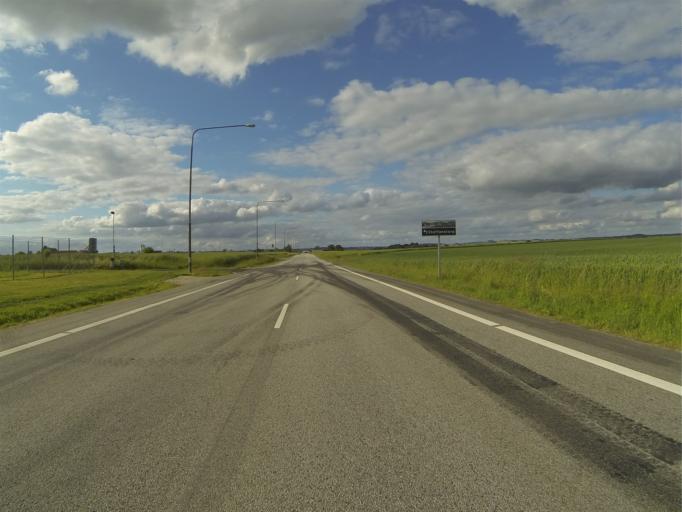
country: SE
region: Skane
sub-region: Staffanstorps Kommun
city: Staffanstorp
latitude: 55.6456
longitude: 13.2375
